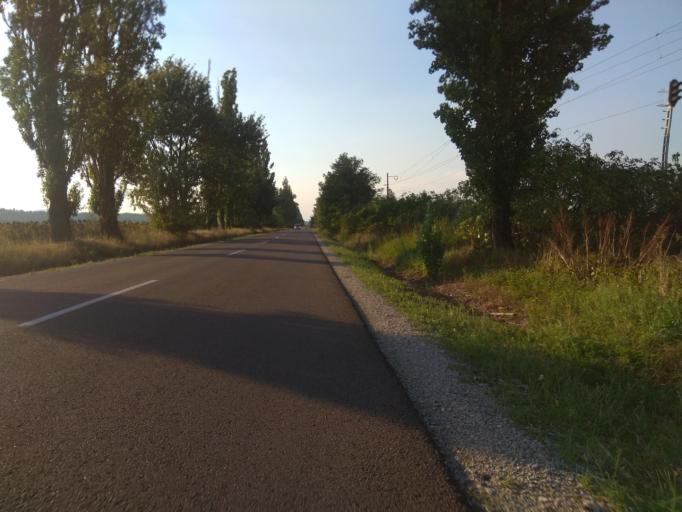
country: HU
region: Borsod-Abauj-Zemplen
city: Nyekladhaza
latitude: 47.9745
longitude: 20.8500
